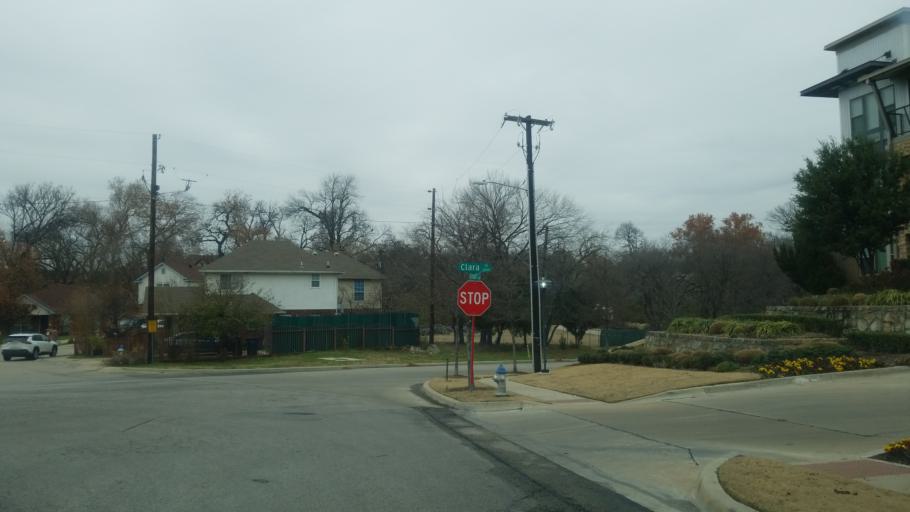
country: US
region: Texas
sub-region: Dallas County
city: Dallas
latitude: 32.8151
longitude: -96.8253
